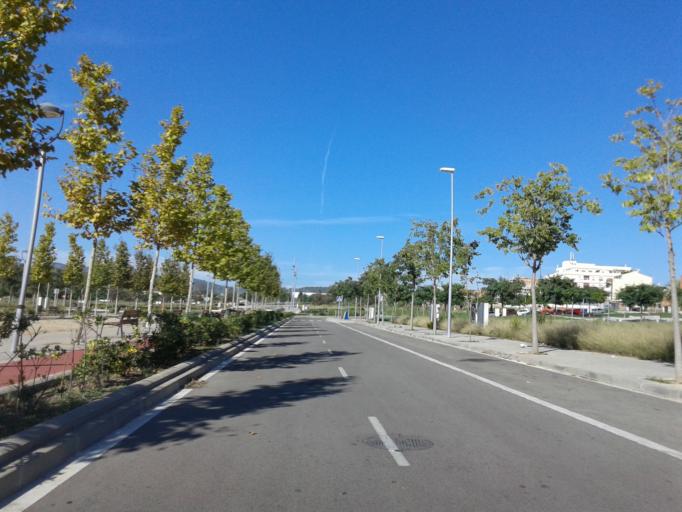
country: ES
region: Catalonia
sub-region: Provincia de Barcelona
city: Vilanova i la Geltru
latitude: 41.2336
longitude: 1.7257
